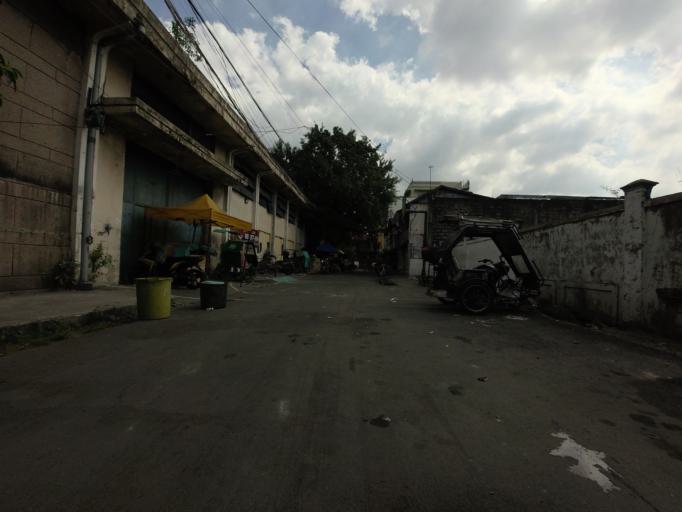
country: PH
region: Metro Manila
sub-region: City of Manila
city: Port Area
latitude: 14.5881
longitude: 120.9754
